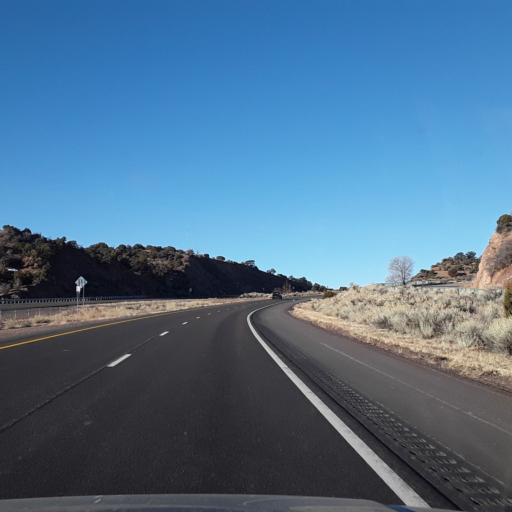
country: US
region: New Mexico
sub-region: Santa Fe County
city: Eldorado at Santa Fe
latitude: 35.5380
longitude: -105.8503
